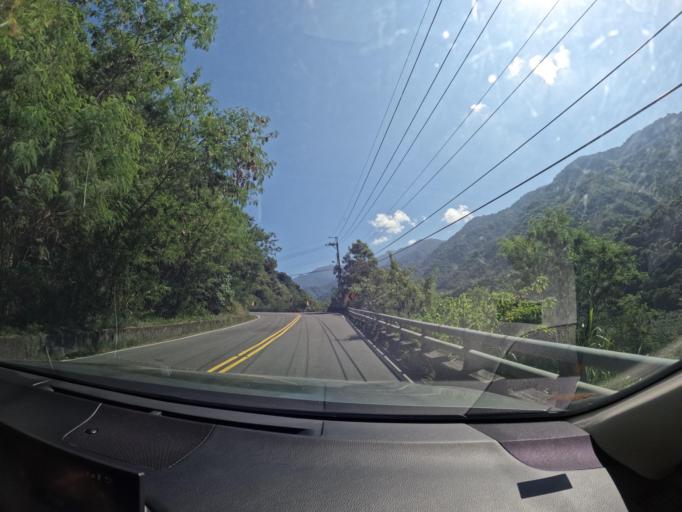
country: TW
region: Taiwan
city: Yujing
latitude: 23.1446
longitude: 120.7503
